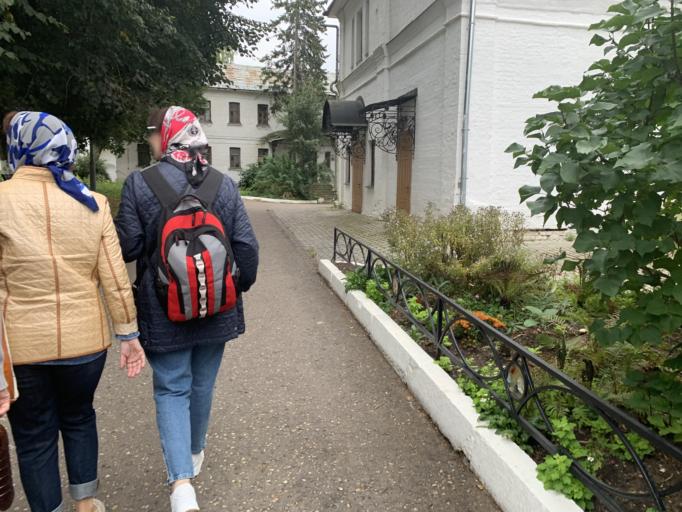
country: RU
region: Moskovskaya
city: Zvenigorod
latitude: 55.7290
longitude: 36.8156
